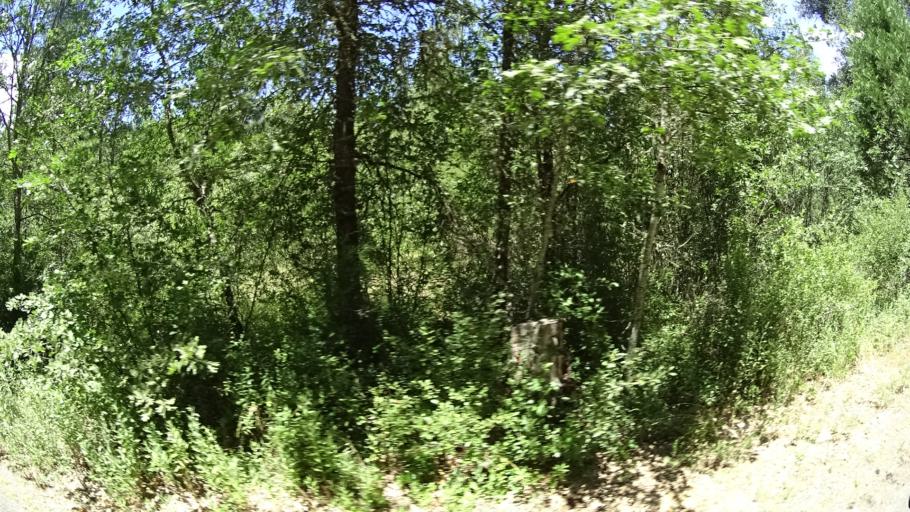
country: US
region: California
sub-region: Calaveras County
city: Arnold
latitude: 38.2555
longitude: -120.4237
